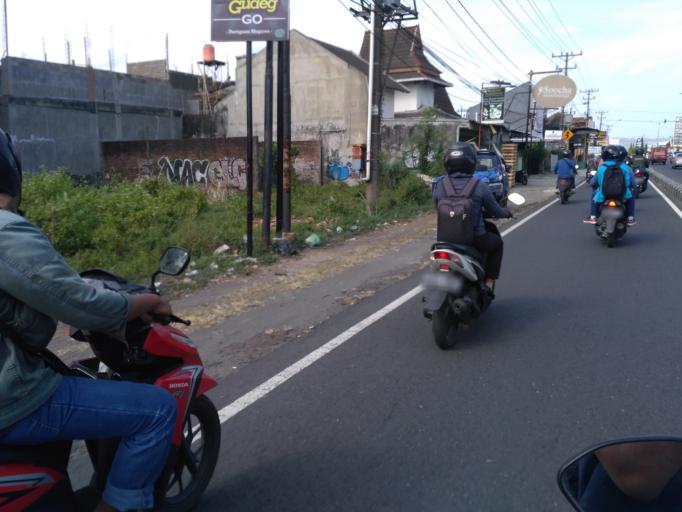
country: ID
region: Daerah Istimewa Yogyakarta
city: Depok
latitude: -7.7641
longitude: 110.4228
